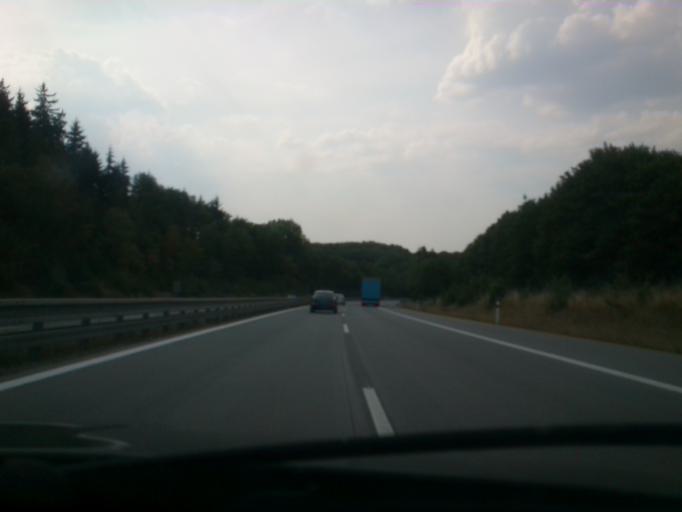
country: CZ
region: Central Bohemia
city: Trhovy Stepanov
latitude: 49.7588
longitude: 14.9613
